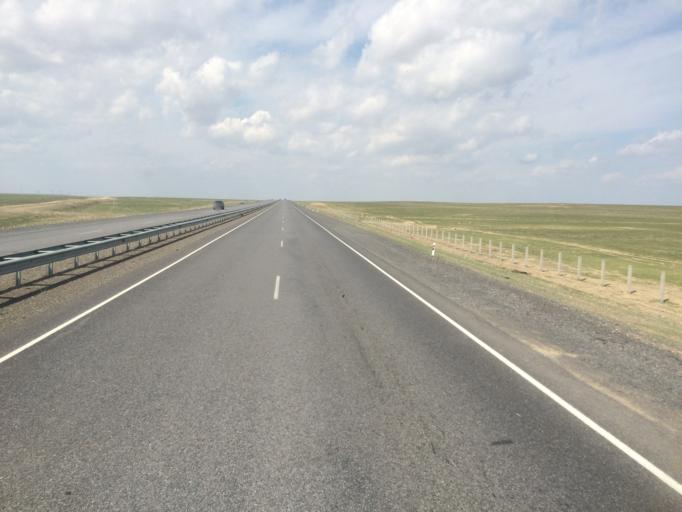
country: KZ
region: Qyzylorda
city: Shalqiya
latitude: 43.8579
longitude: 67.4019
